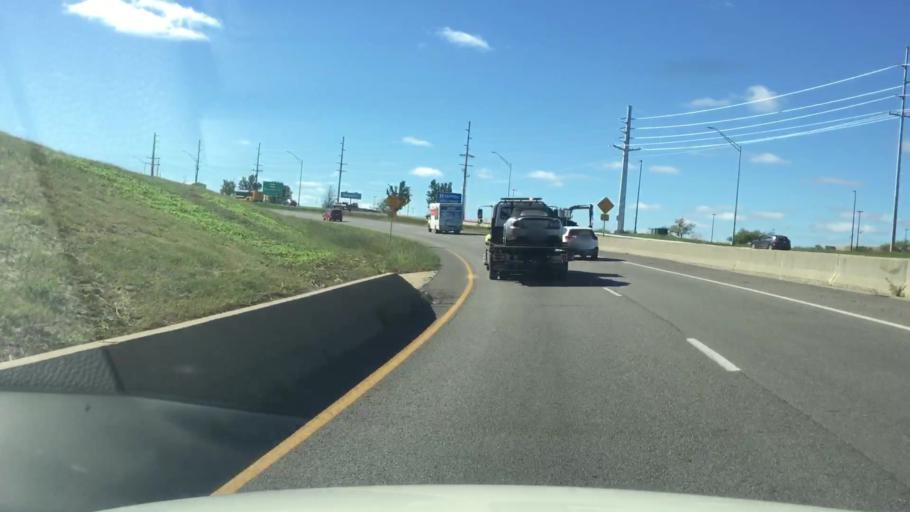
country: US
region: Missouri
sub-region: Boone County
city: Columbia
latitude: 38.9567
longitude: -92.2940
